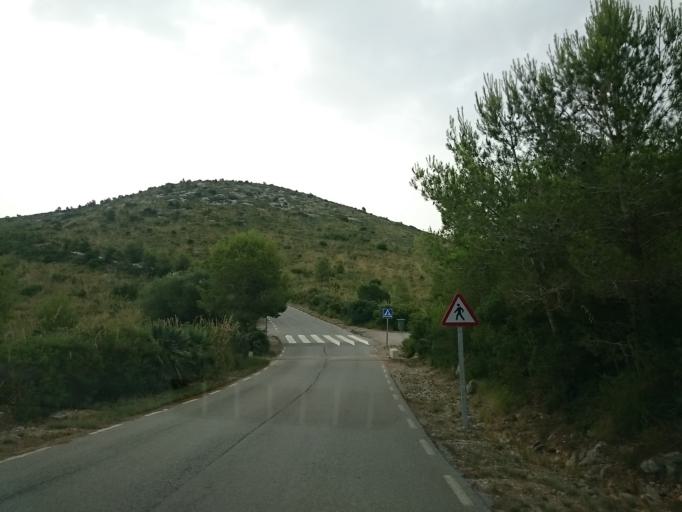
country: ES
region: Catalonia
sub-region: Provincia de Barcelona
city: Olivella
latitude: 41.2795
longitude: 1.8759
